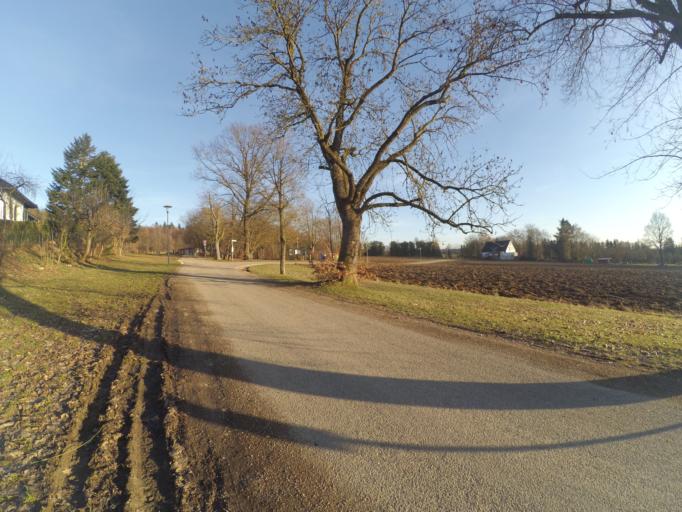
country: DE
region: Bavaria
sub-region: Swabia
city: Guenzburg
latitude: 48.4462
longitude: 10.2993
